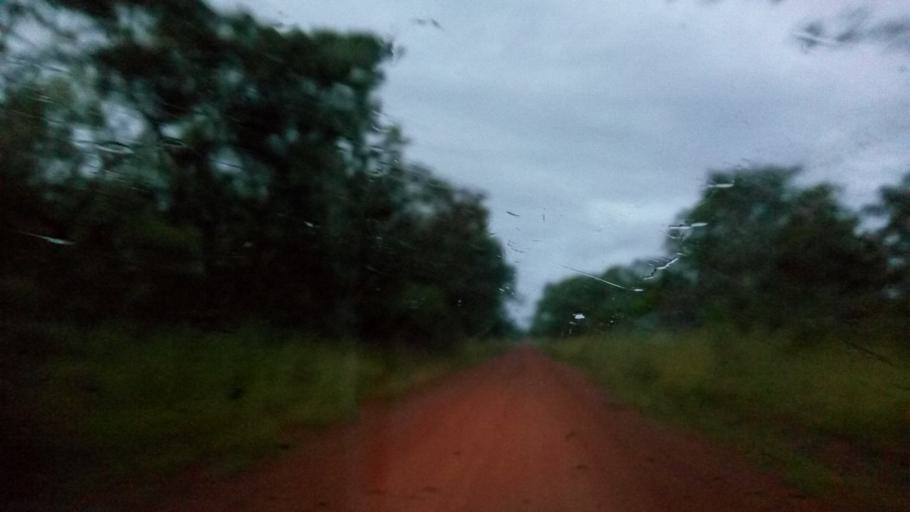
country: ZM
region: Luapula
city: Nchelenge
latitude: -9.8222
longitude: 28.1356
